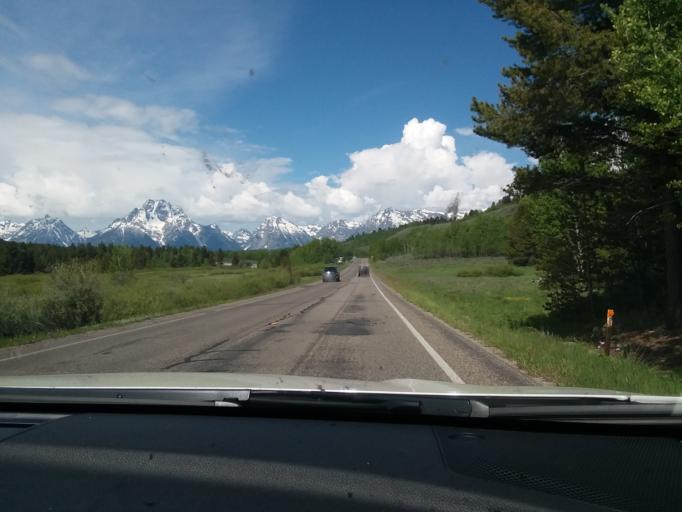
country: US
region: Wyoming
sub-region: Teton County
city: Jackson
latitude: 43.8660
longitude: -110.5432
